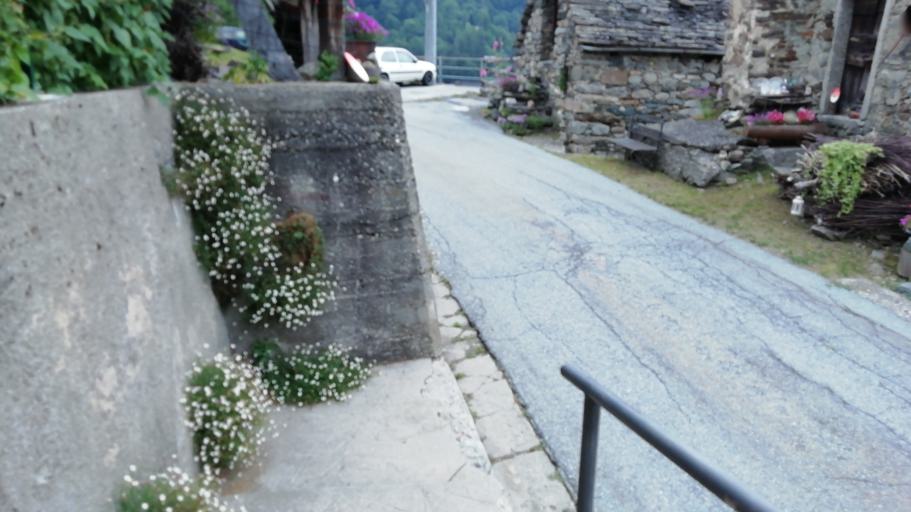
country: IT
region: Piedmont
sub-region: Provincia Verbano-Cusio-Ossola
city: San Lorenzo
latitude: 46.1268
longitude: 8.2020
